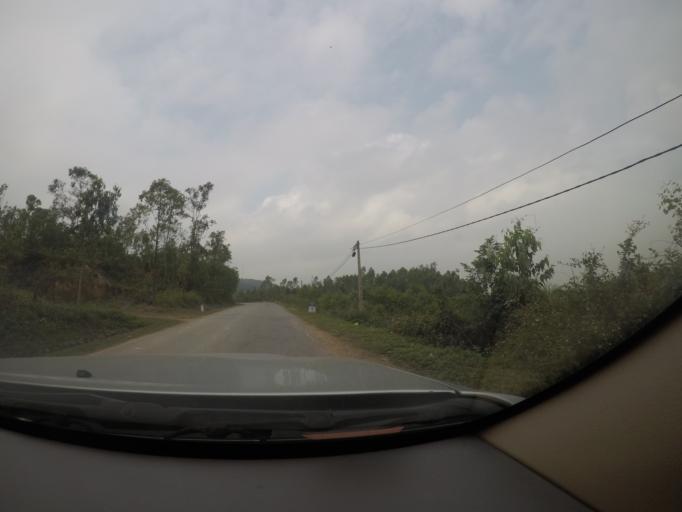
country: VN
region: Quang Binh
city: Ba Don
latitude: 17.6899
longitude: 106.4314
